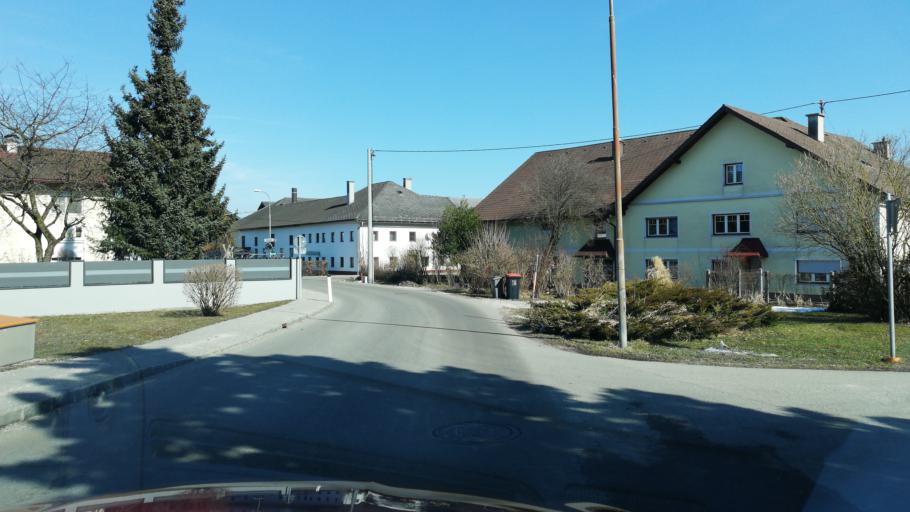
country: AT
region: Upper Austria
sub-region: Politischer Bezirk Vocklabruck
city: Vocklabruck
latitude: 47.9872
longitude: 13.6576
